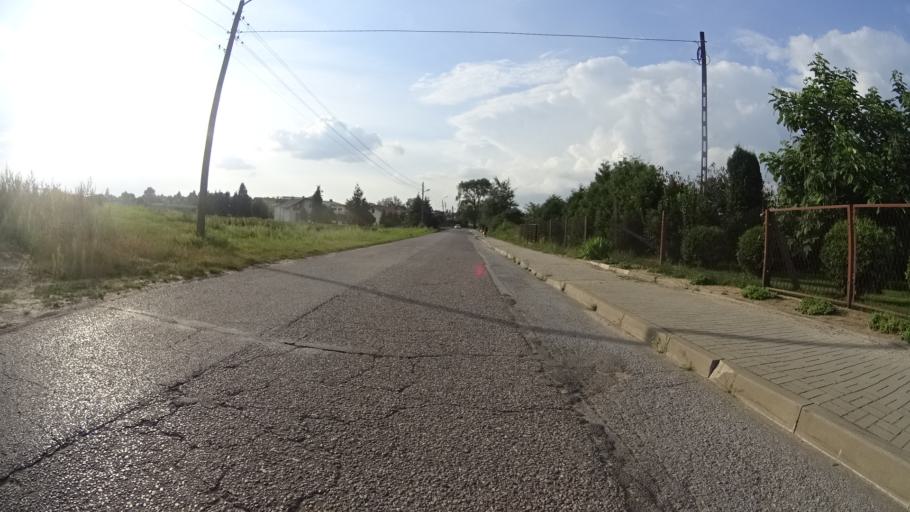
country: PL
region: Masovian Voivodeship
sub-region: Powiat grojecki
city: Mogielnica
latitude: 51.6873
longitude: 20.7287
